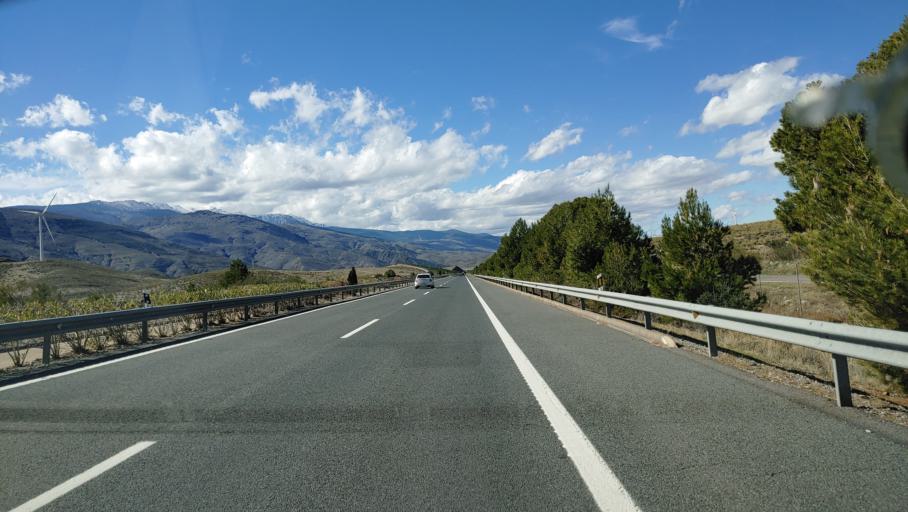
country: ES
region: Andalusia
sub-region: Provincia de Almeria
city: Abla
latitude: 37.1387
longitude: -2.6739
